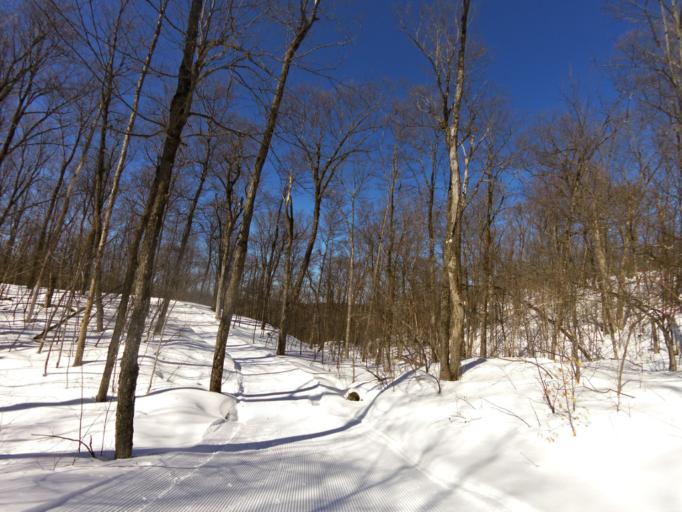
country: CA
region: Quebec
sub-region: Outaouais
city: Wakefield
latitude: 45.5044
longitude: -75.8666
